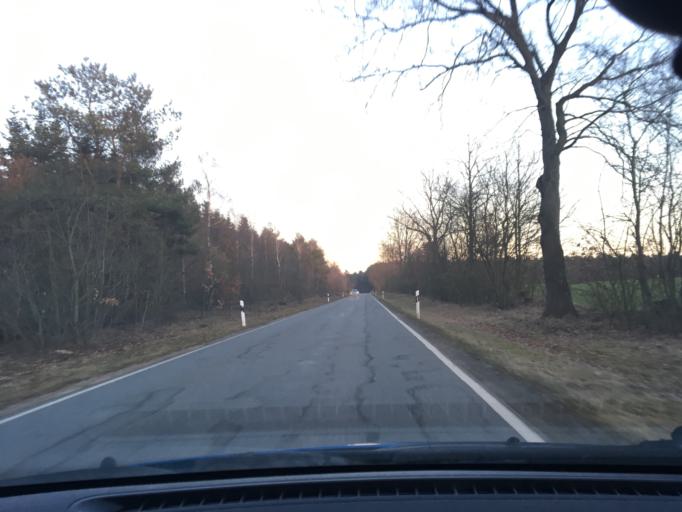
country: DE
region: Schleswig-Holstein
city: Brothen
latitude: 53.4851
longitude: 10.6790
